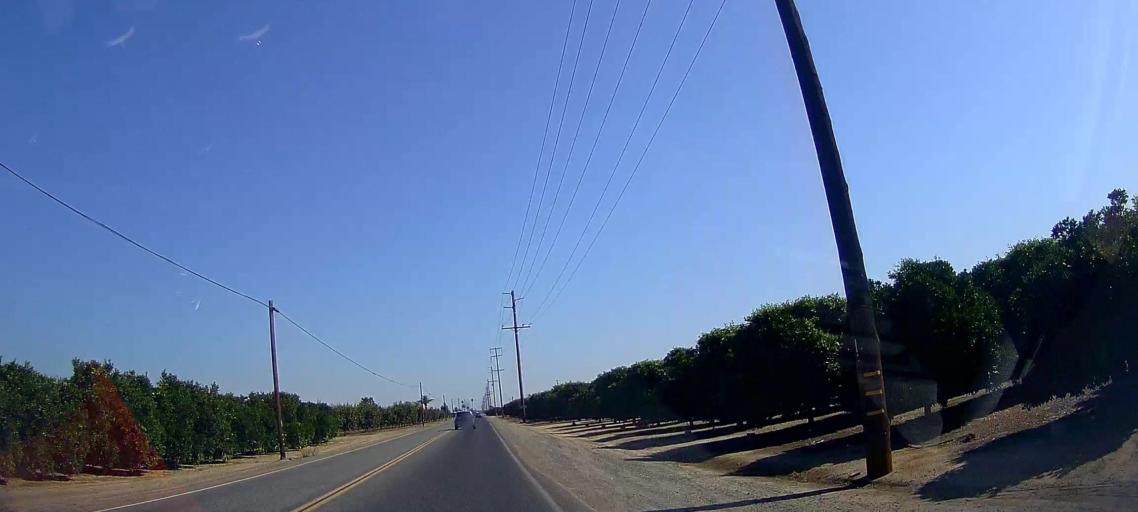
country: US
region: California
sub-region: Tulare County
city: Exeter
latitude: 36.2584
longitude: -119.1183
